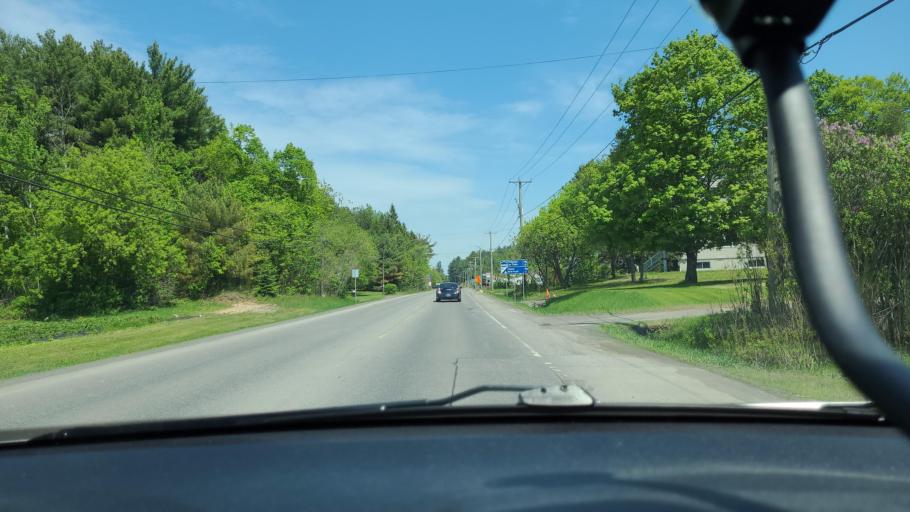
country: CA
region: Quebec
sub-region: Laurentides
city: Lachute
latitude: 45.6636
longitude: -74.2997
